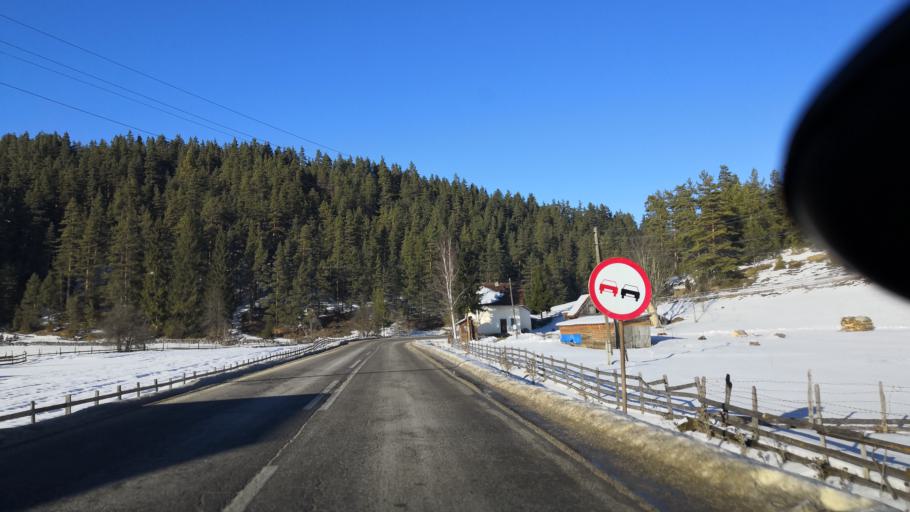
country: BA
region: Republika Srpska
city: Sokolac
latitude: 43.9778
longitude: 18.8581
